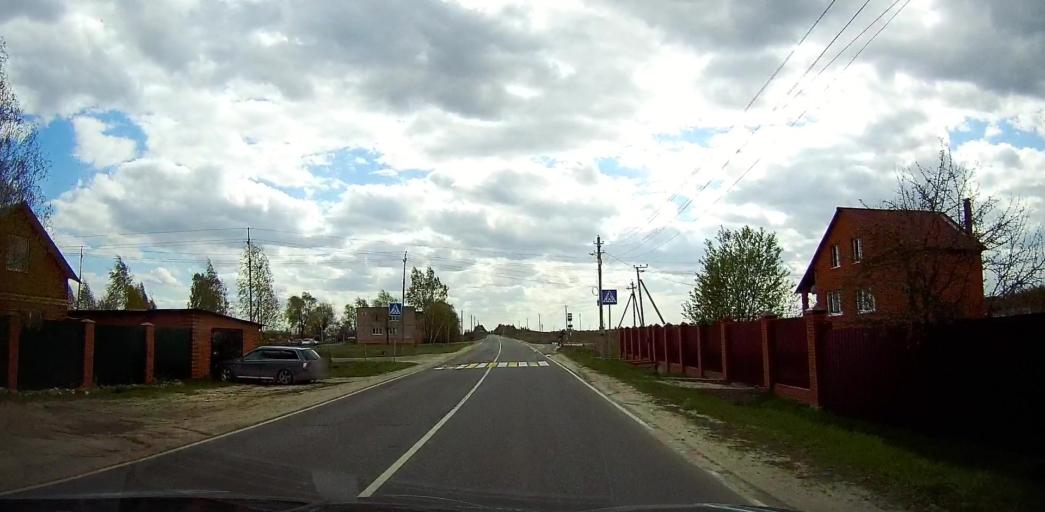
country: RU
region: Moskovskaya
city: Davydovo
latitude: 55.6437
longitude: 38.7503
